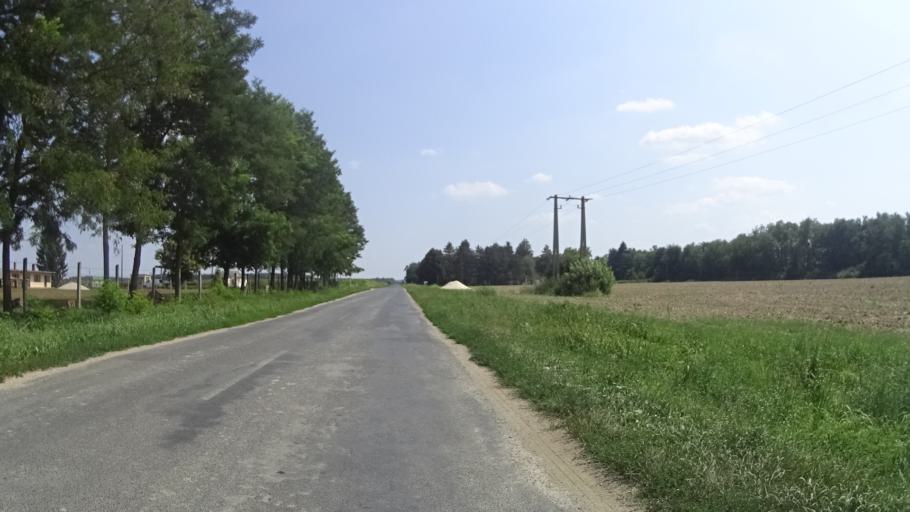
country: HR
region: Medimurska
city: Kotoriba
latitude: 46.3799
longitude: 16.8431
